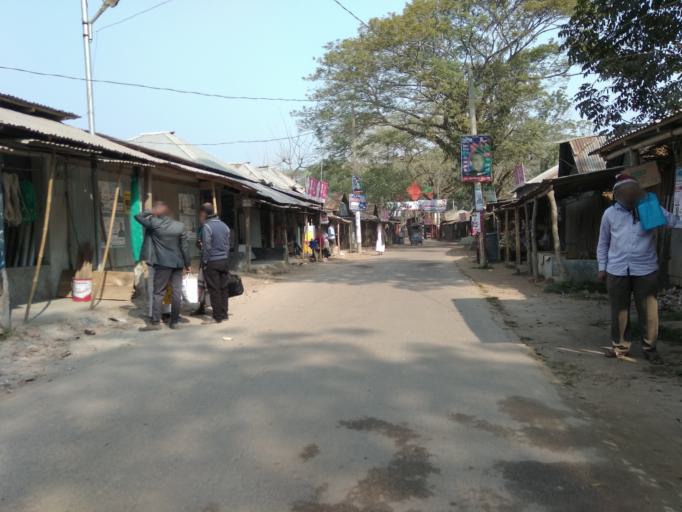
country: BD
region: Barisal
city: Mehendiganj
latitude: 22.9557
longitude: 90.4148
